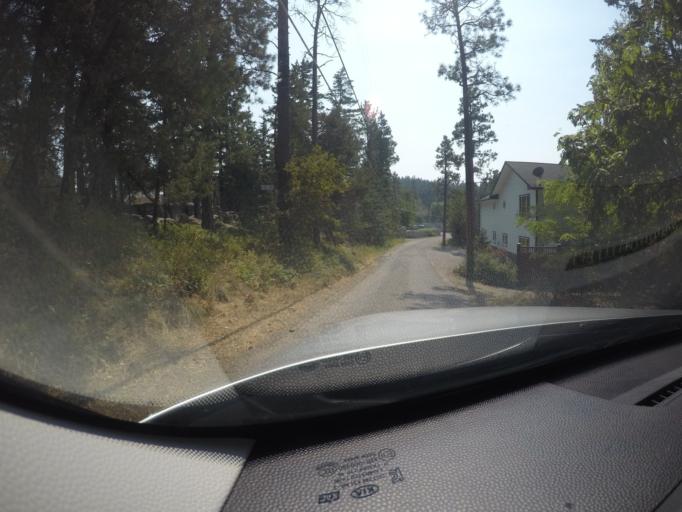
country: US
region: Montana
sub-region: Lake County
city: Polson
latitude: 47.7643
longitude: -114.1418
